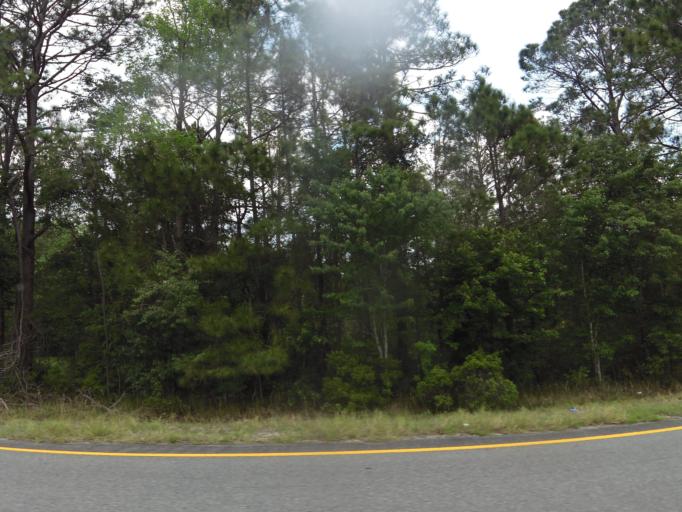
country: US
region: Georgia
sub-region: Charlton County
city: Folkston
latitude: 30.8708
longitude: -82.0149
